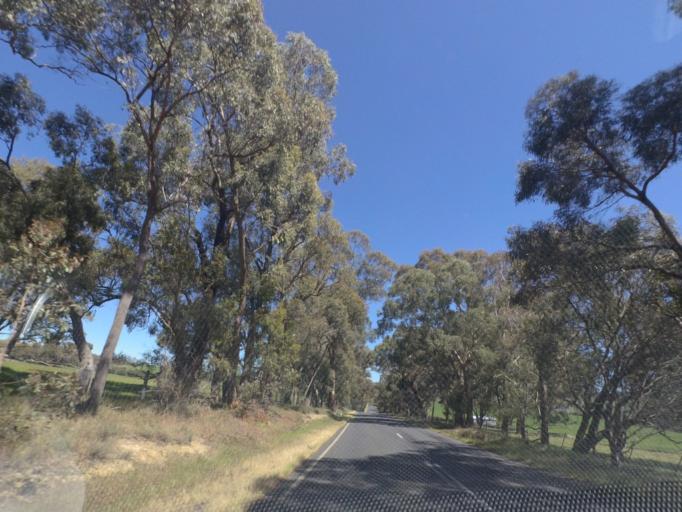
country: AU
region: Victoria
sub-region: Whittlesea
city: Whittlesea
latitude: -37.2658
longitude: 145.0426
